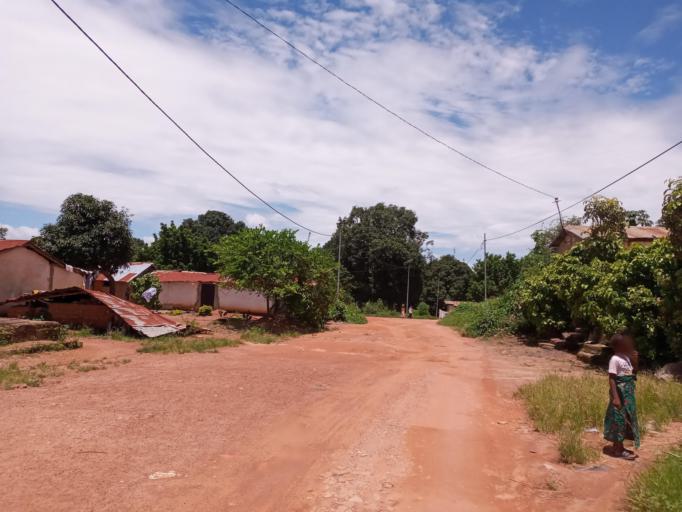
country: SL
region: Eastern Province
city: Koidu
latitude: 8.6481
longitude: -10.9637
